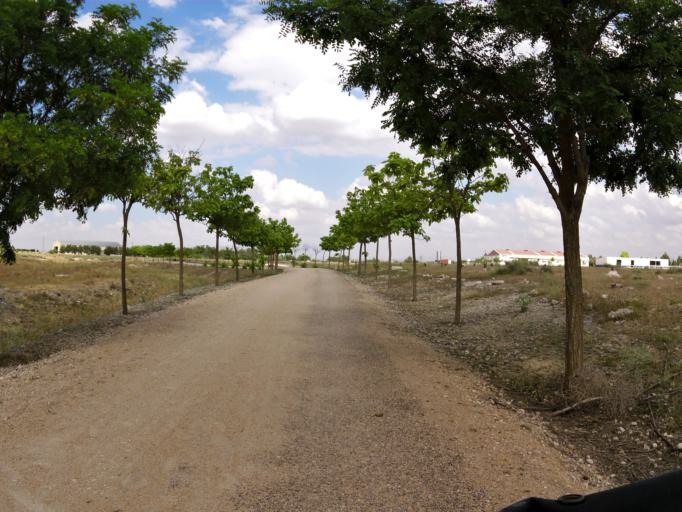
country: ES
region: Castille-La Mancha
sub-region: Provincia de Albacete
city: Albacete
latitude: 38.9610
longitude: -1.9636
